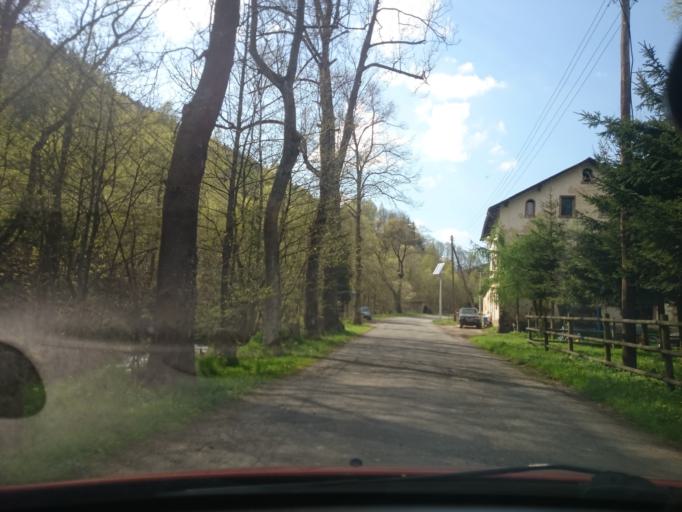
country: PL
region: Lower Silesian Voivodeship
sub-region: Powiat klodzki
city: Bystrzyca Klodzka
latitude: 50.2982
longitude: 16.5446
